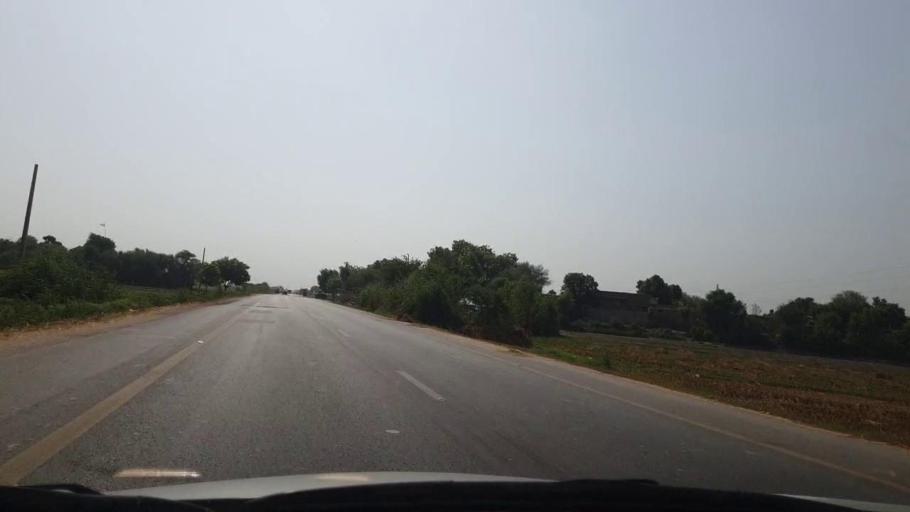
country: PK
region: Sindh
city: Tando Muhammad Khan
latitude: 25.1197
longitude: 68.5715
